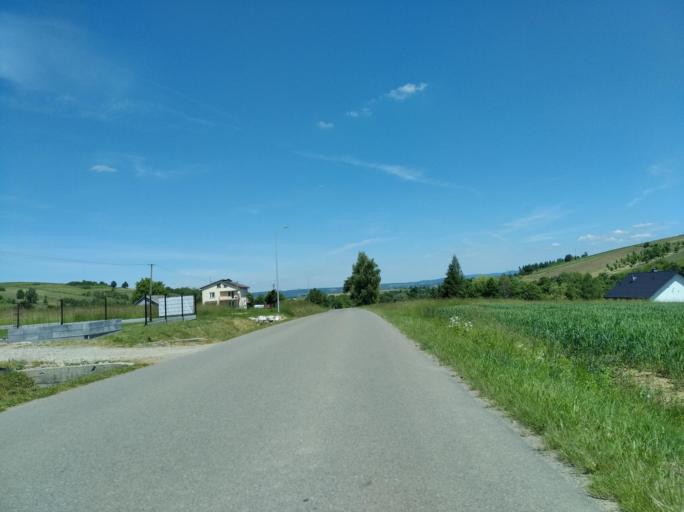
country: PL
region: Subcarpathian Voivodeship
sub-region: Powiat jasielski
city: Tarnowiec
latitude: 49.6819
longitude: 21.5436
